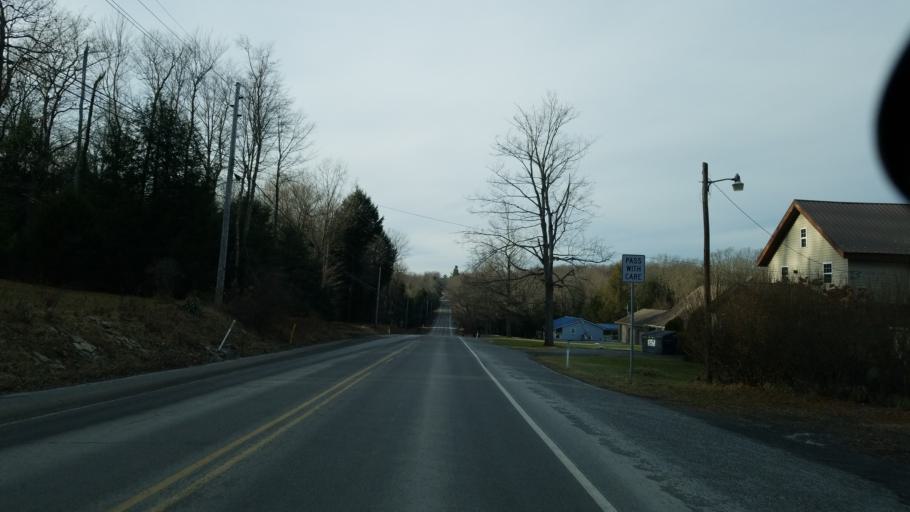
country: US
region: Pennsylvania
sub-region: Clearfield County
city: DuBois
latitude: 41.0248
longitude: -78.6669
